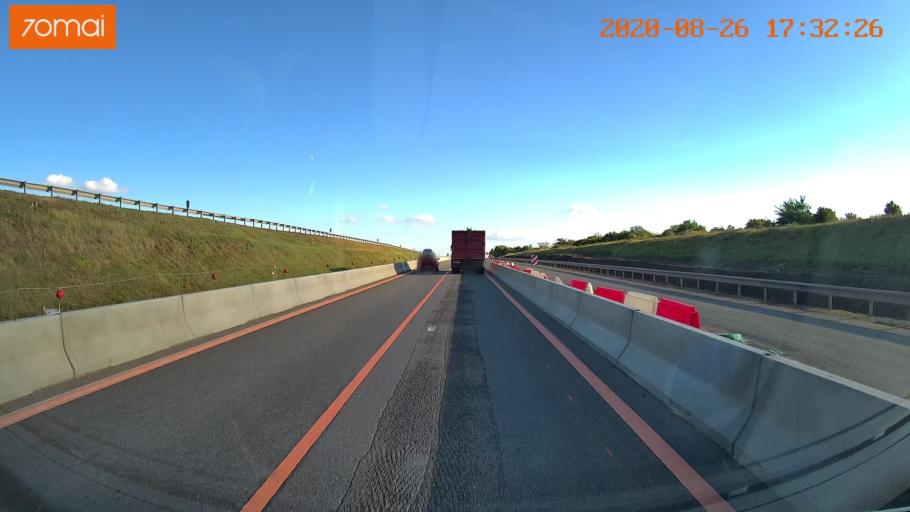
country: RU
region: Tula
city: Kazachka
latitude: 53.4222
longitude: 38.1809
